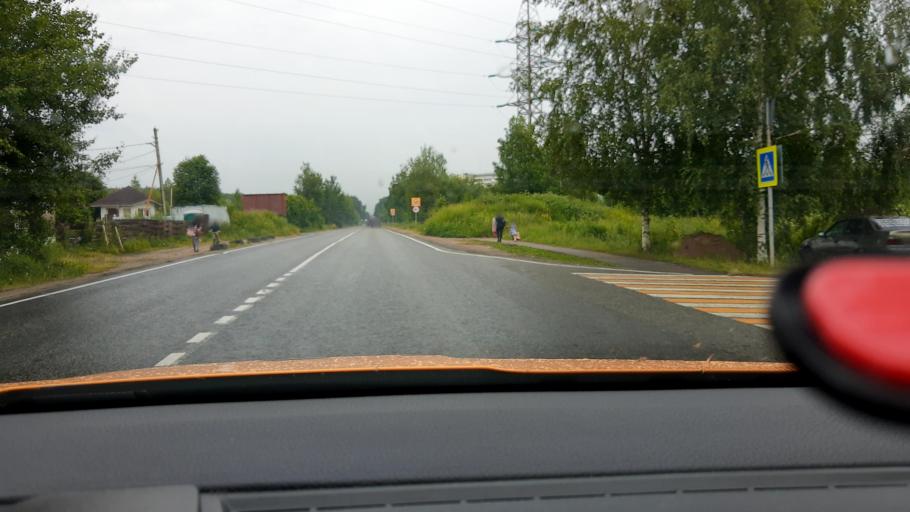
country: RU
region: Moskovskaya
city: Povedniki
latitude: 55.9930
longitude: 37.6650
